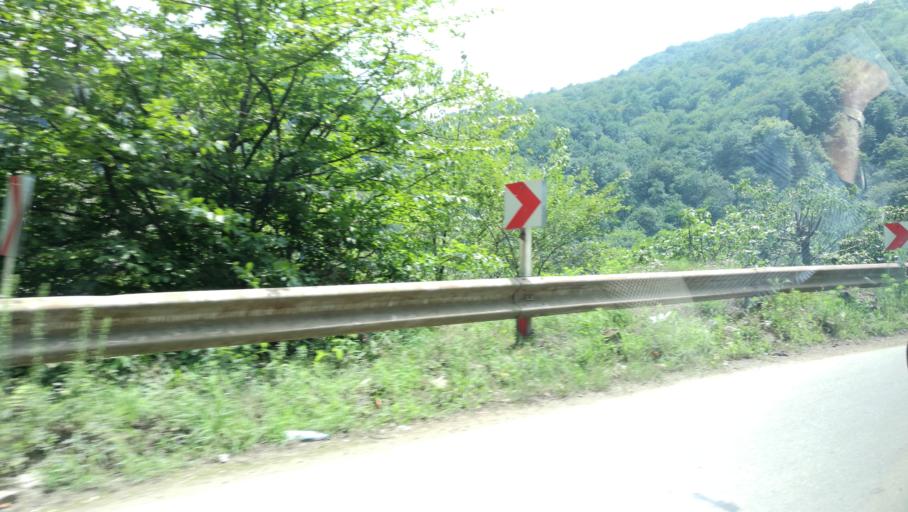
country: IR
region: Mazandaran
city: Ramsar
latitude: 36.8933
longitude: 50.5798
